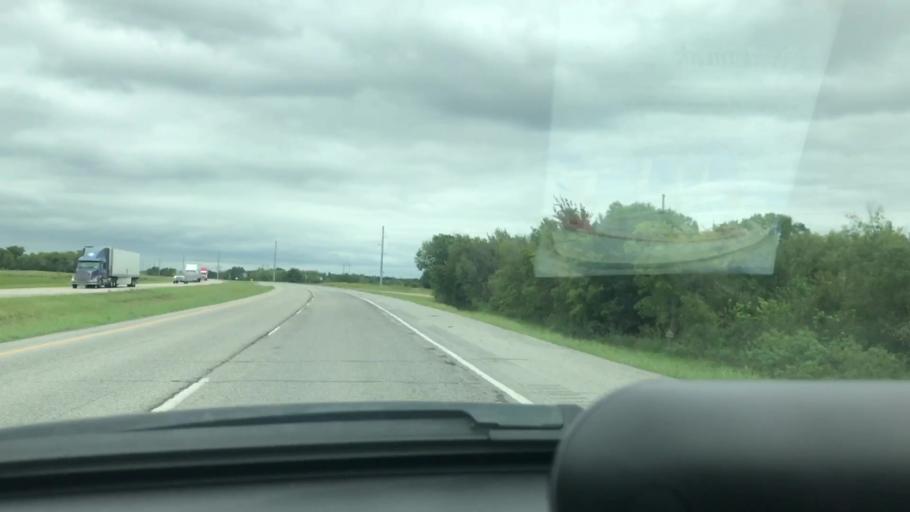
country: US
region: Oklahoma
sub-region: Wagoner County
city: Wagoner
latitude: 35.9953
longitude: -95.3695
